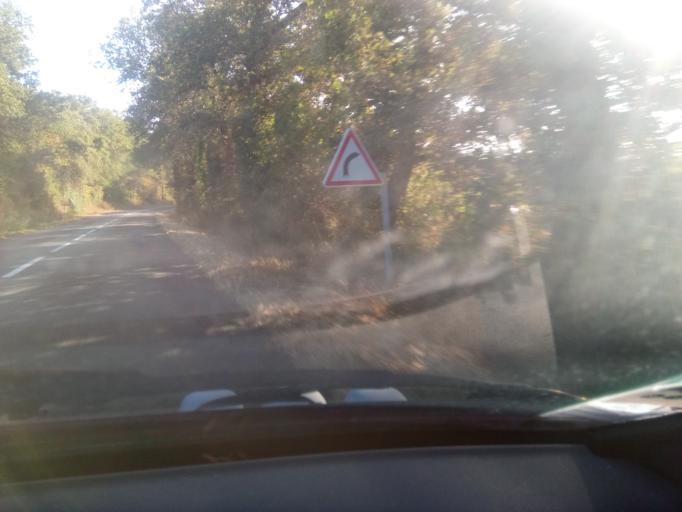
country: FR
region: Poitou-Charentes
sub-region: Departement de la Vienne
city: Lussac-les-Chateaux
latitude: 46.3236
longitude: 0.7085
